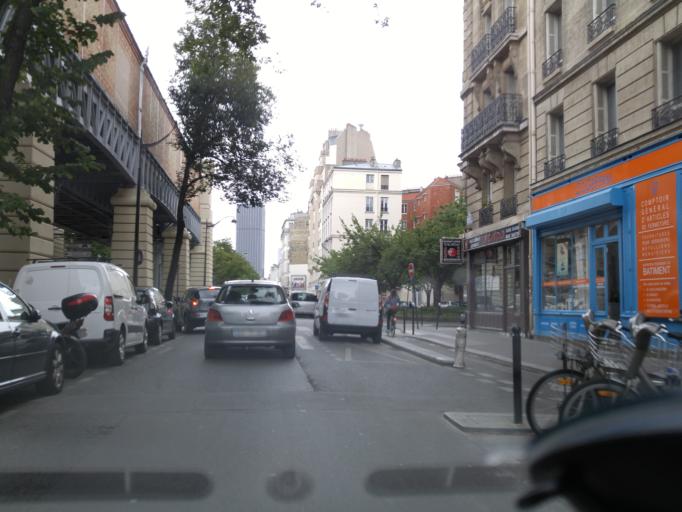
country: FR
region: Ile-de-France
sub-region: Departement des Hauts-de-Seine
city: Vanves
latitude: 48.8475
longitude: 2.3025
